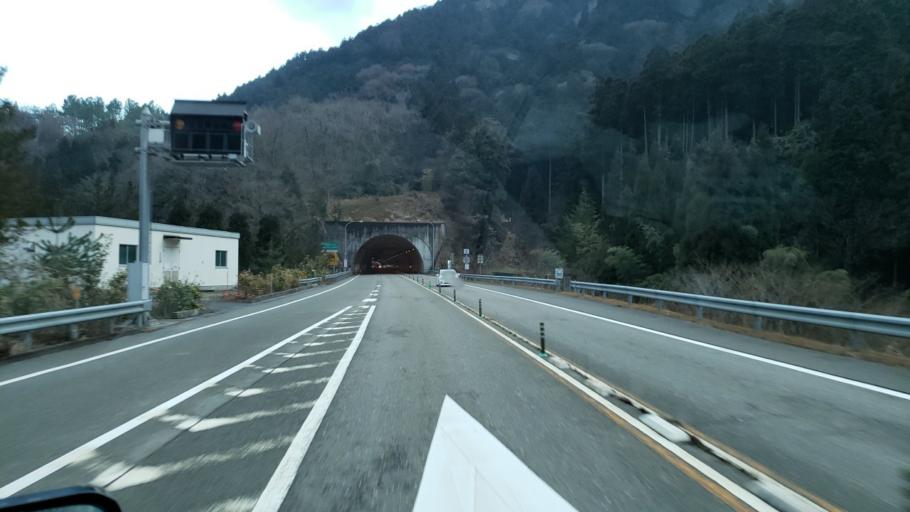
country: JP
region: Hyogo
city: Nishiwaki
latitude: 35.2262
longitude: 134.7858
